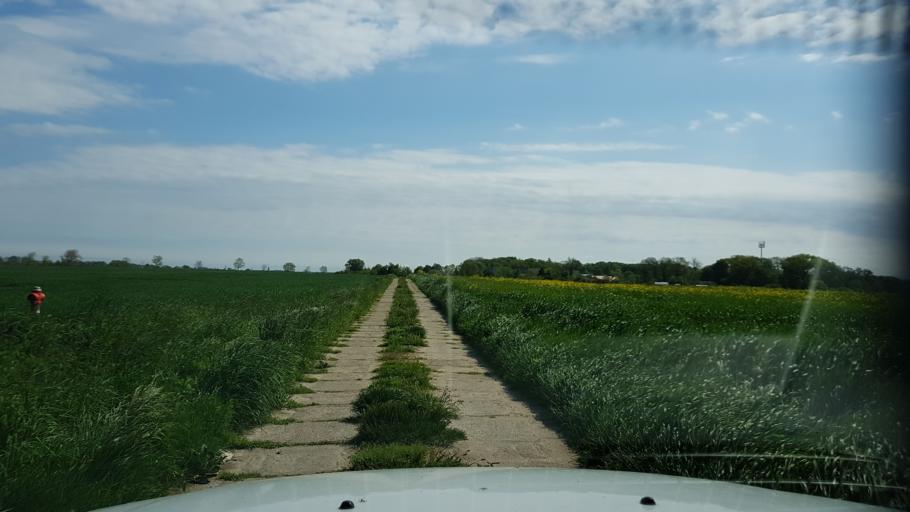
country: PL
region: West Pomeranian Voivodeship
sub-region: Powiat koszalinski
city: Mielno
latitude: 54.2371
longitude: 15.9118
